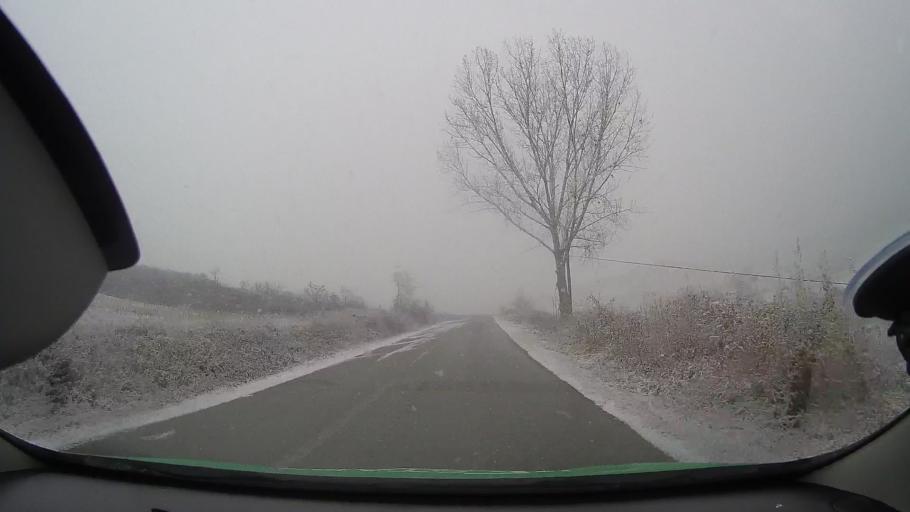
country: RO
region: Alba
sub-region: Comuna Hoparta
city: Hoparta
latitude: 46.3079
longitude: 23.8555
